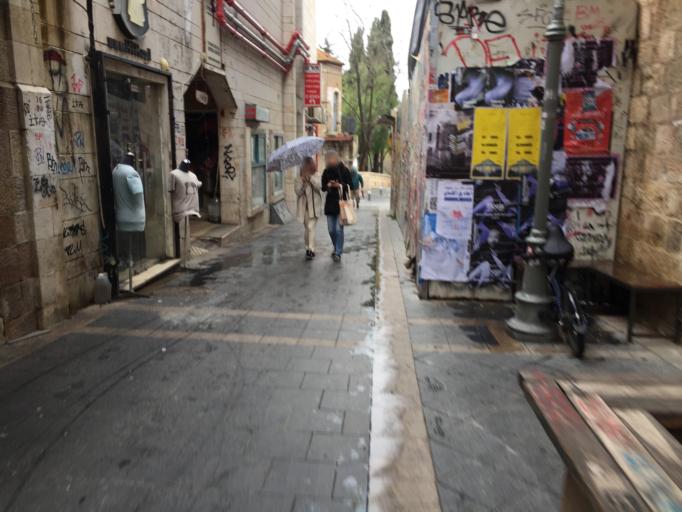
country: IL
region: Jerusalem
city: West Jerusalem
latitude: 31.7795
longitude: 35.2218
